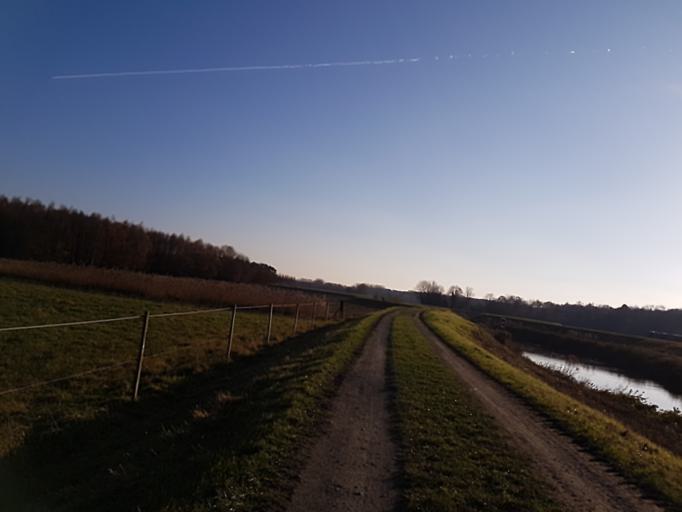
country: BE
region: Flanders
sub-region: Provincie Vlaams-Brabant
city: Boortmeerbeek
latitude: 50.9978
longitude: 4.5991
